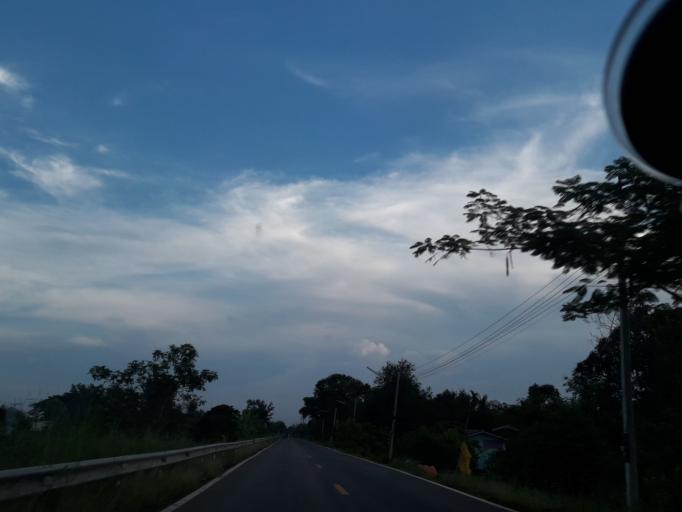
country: TH
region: Sara Buri
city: Nong Khae
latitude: 14.2866
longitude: 100.8911
